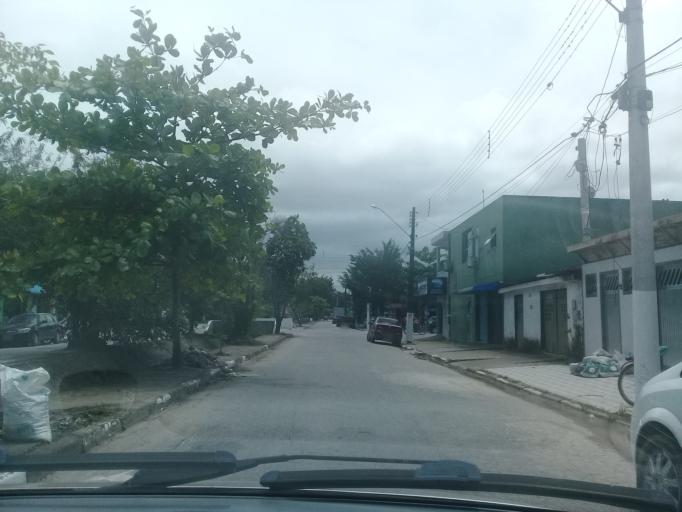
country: BR
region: Sao Paulo
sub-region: Guaruja
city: Guaruja
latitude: -23.9655
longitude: -46.2540
